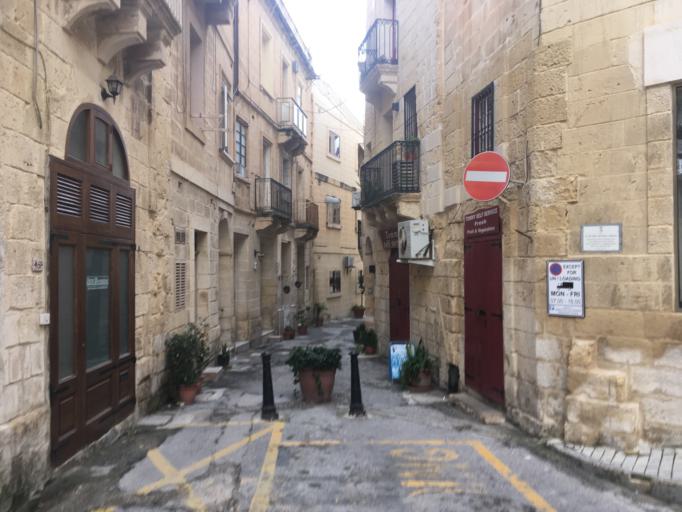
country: MT
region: L-Isla
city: Senglea
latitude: 35.8882
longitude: 14.5216
